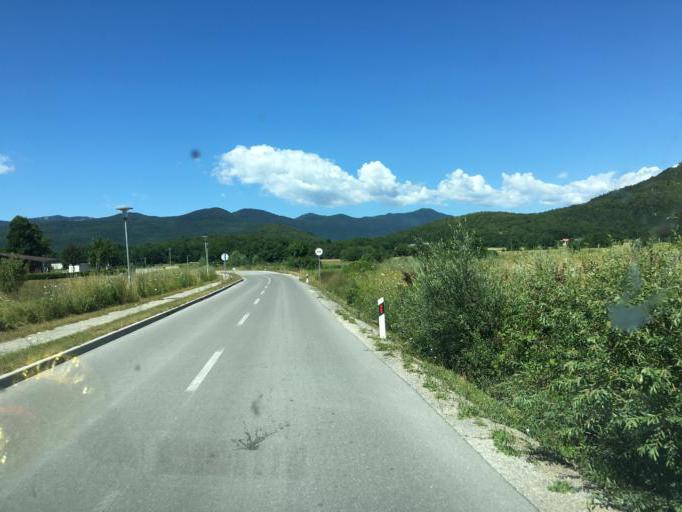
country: HR
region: Licko-Senjska
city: Gospic
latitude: 44.5608
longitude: 15.3096
